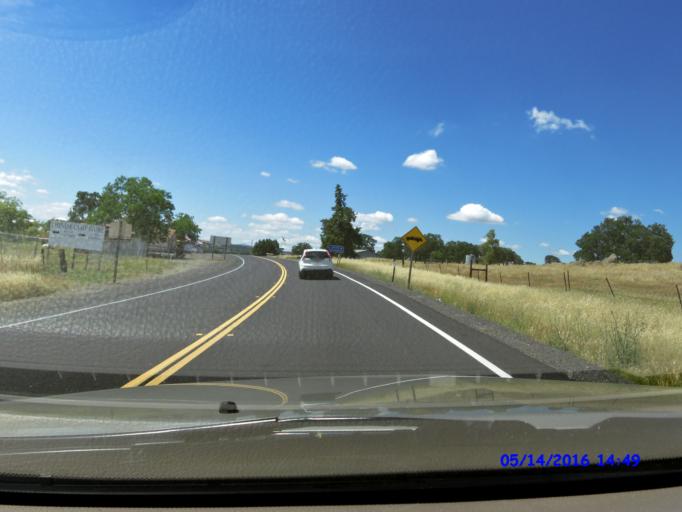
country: US
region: California
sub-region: Tuolumne County
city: Jamestown
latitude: 37.8721
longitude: -120.4314
